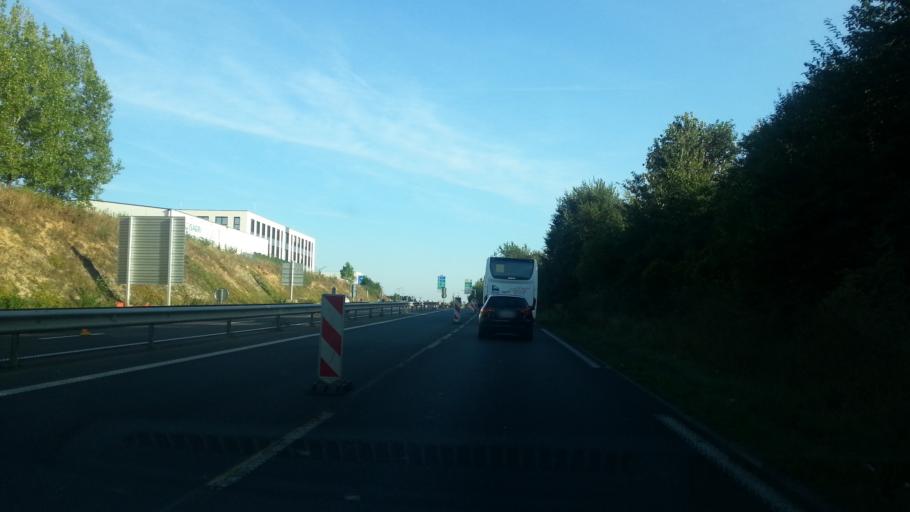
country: FR
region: Picardie
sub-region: Departement de l'Oise
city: Tille
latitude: 49.4557
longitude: 2.0937
